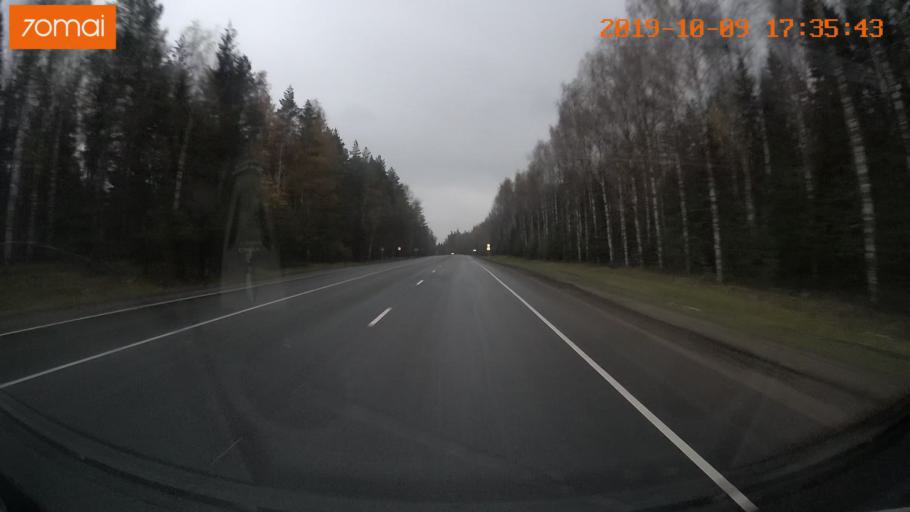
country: RU
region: Ivanovo
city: Bogorodskoye
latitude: 57.0893
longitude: 41.0002
